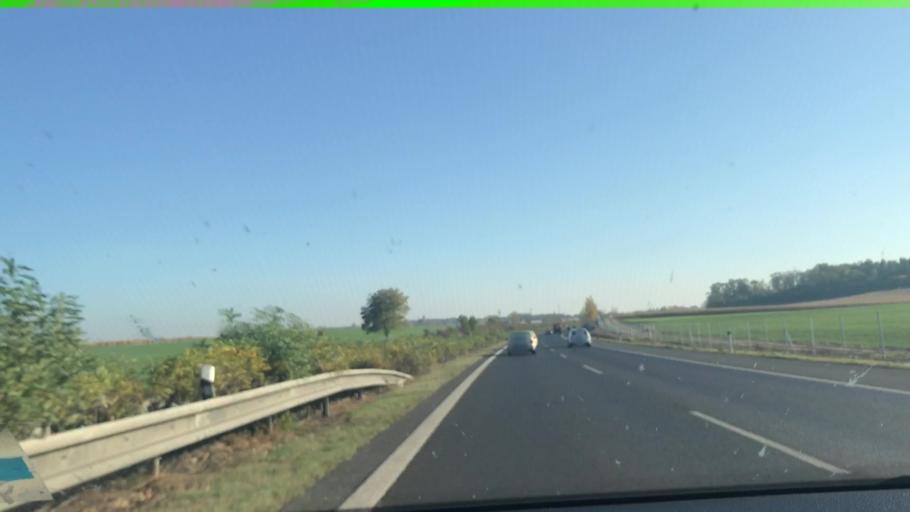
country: CZ
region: Ustecky
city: Roudnice nad Labem
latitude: 50.3558
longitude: 14.2729
